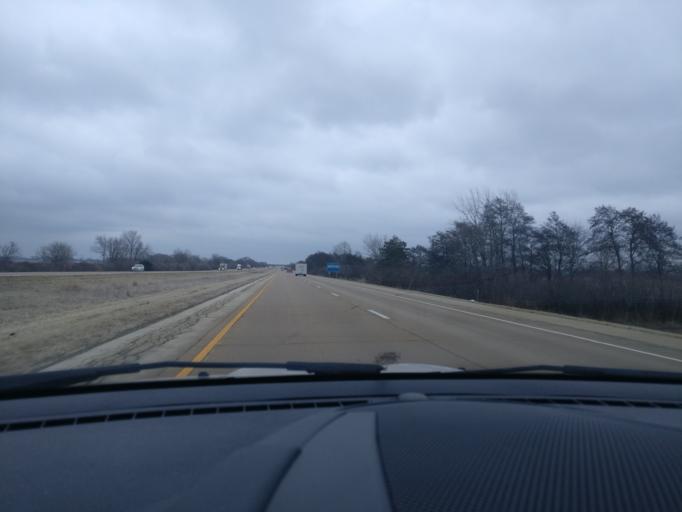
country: US
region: Illinois
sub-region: Whiteside County
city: Rock Falls
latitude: 41.7512
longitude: -89.7230
